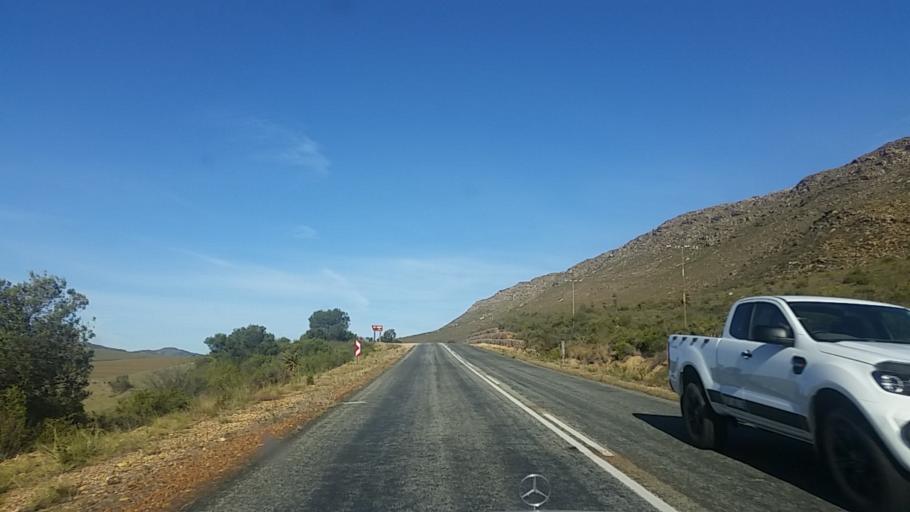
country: ZA
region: Western Cape
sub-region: Eden District Municipality
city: Knysna
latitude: -33.7427
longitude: 23.0140
